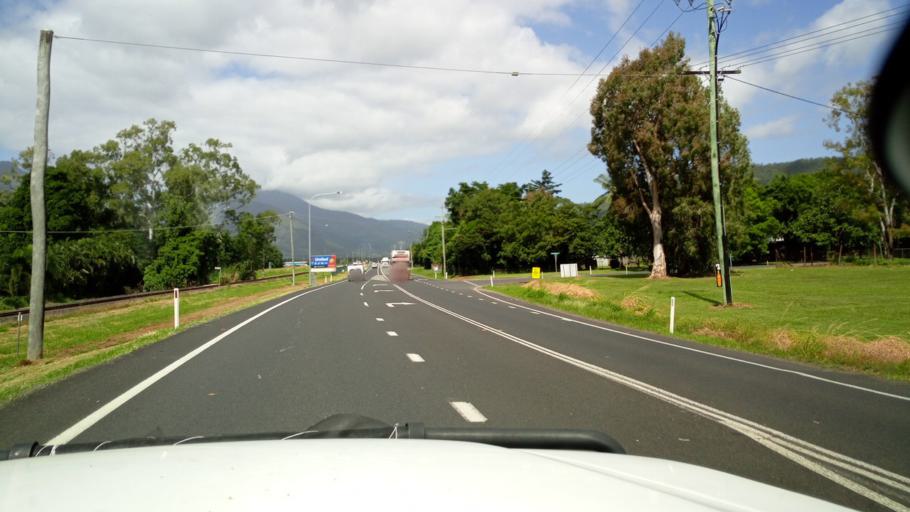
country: AU
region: Queensland
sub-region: Cairns
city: Woree
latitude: -17.0758
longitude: 145.7756
